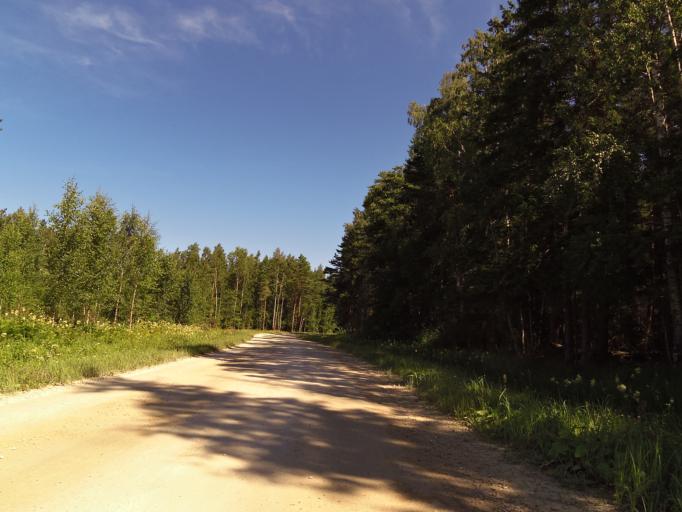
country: EE
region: Hiiumaa
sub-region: Kaerdla linn
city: Kardla
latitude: 58.9291
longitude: 22.3722
